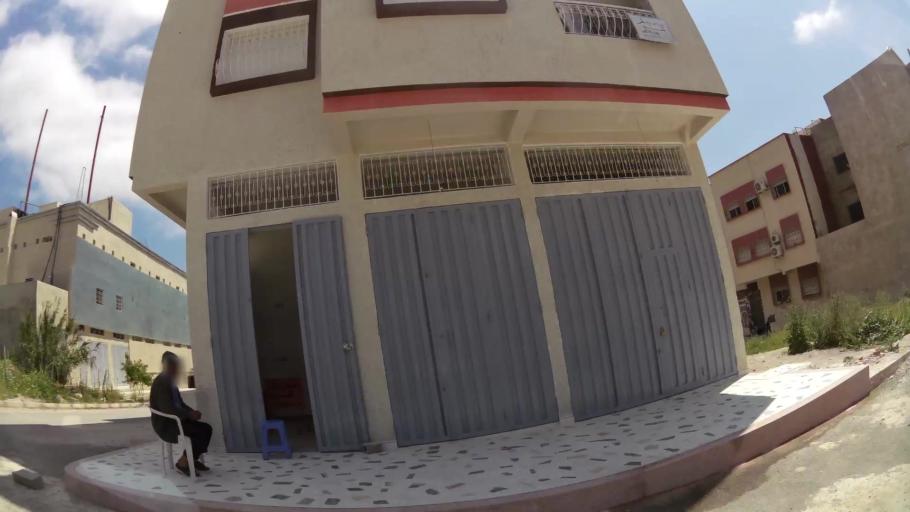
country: MA
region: Fes-Boulemane
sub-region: Fes
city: Fes
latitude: 34.0579
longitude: -5.0387
